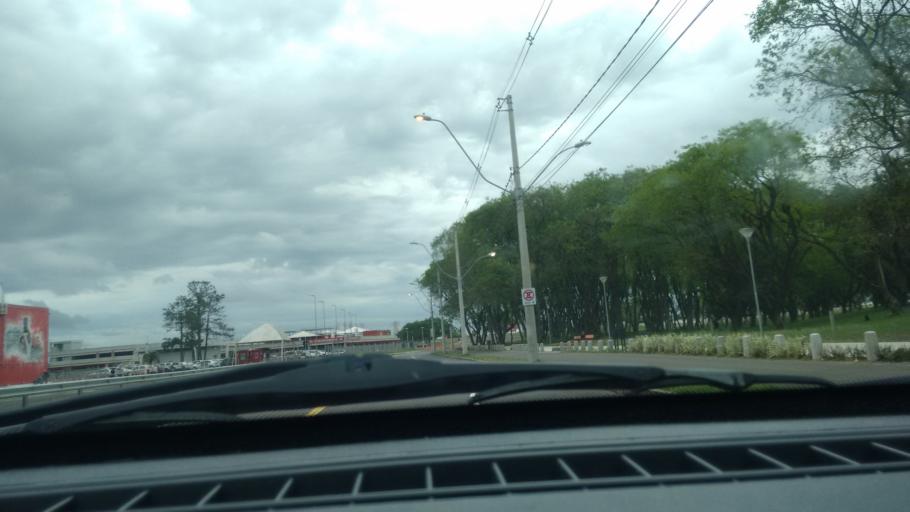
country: BR
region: Rio Grande do Sul
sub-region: Porto Alegre
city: Porto Alegre
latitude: -30.0636
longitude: -51.2344
